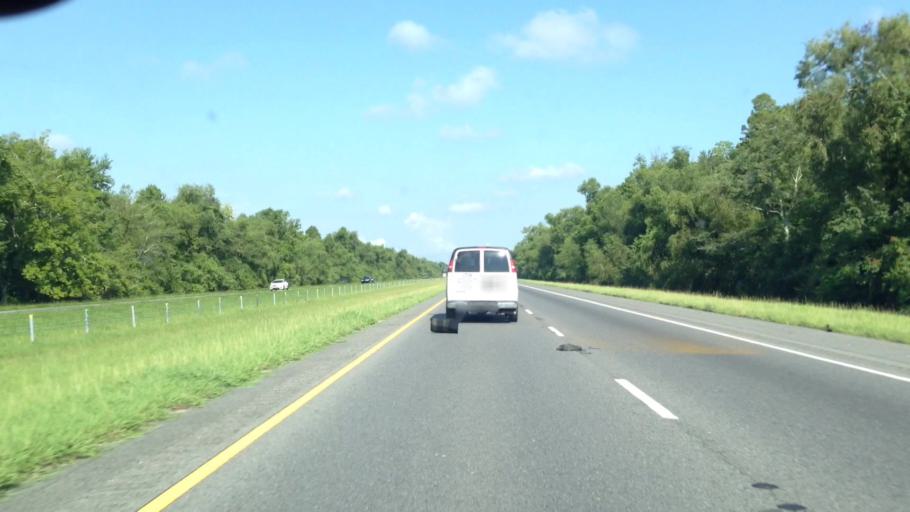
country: US
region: Louisiana
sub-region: Saint James Parish
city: Grand Point
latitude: 30.1358
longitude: -90.7332
